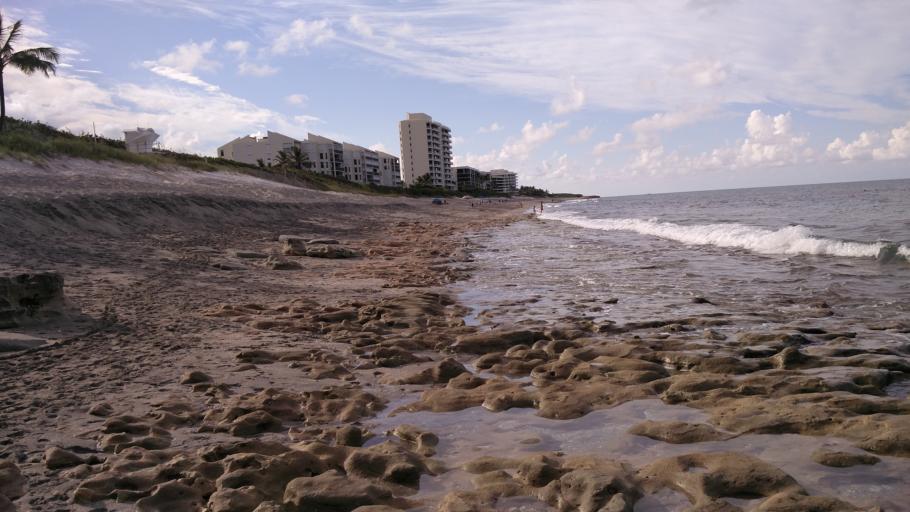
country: US
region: Florida
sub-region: Palm Beach County
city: Jupiter
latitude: 26.9629
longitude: -80.0779
